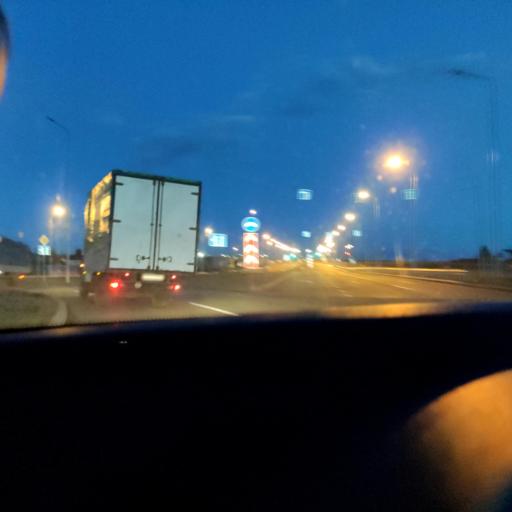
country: RU
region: Samara
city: Petra-Dubrava
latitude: 53.2943
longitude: 50.3282
